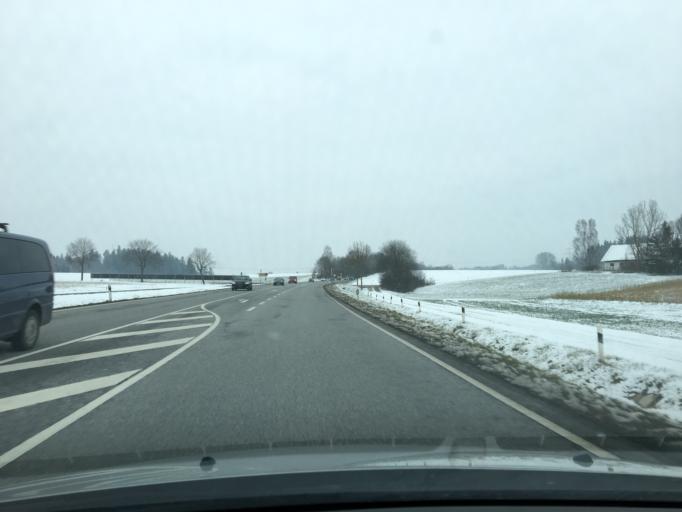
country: DE
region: Bavaria
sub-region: Lower Bavaria
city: Geisenhausen
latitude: 48.4842
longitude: 12.2458
